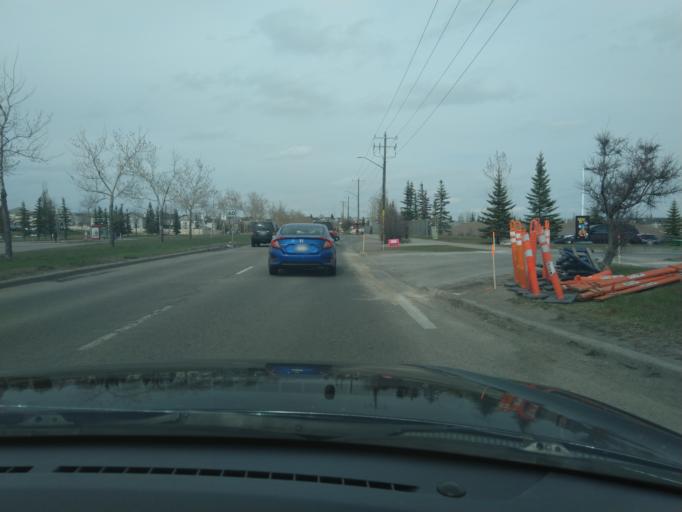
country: CA
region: Alberta
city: Calgary
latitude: 51.1425
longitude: -114.0687
